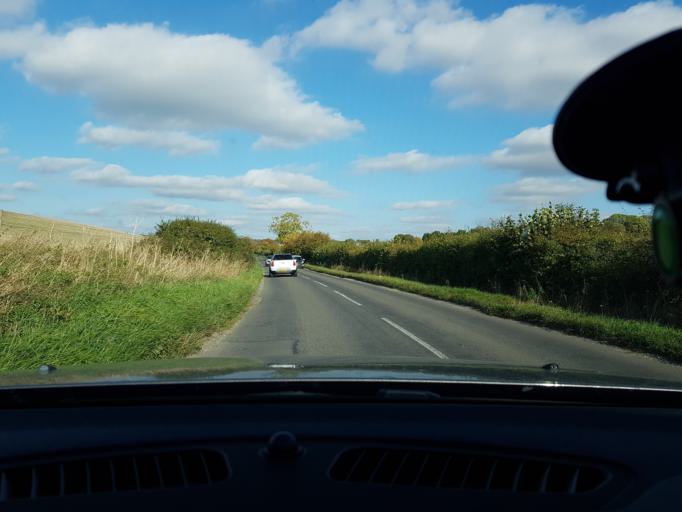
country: GB
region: England
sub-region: West Berkshire
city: Lambourn
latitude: 51.5018
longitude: -1.5446
